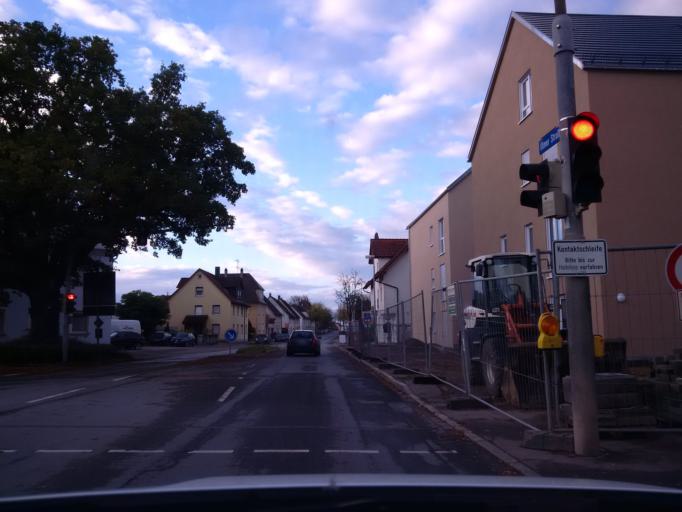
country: DE
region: Baden-Wuerttemberg
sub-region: Tuebingen Region
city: Laupheim
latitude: 48.2355
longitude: 9.8816
